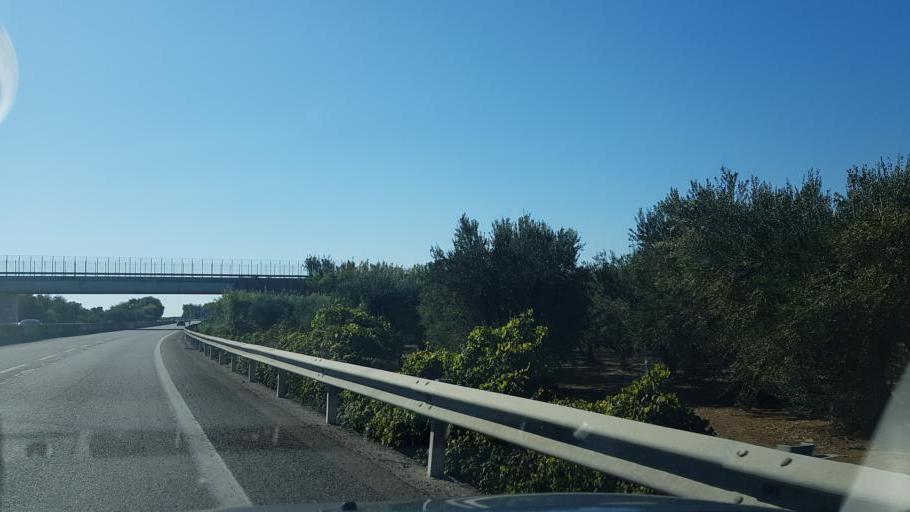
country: IT
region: Apulia
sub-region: Provincia di Brindisi
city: San Pietro Vernotico
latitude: 40.5119
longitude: 18.0234
